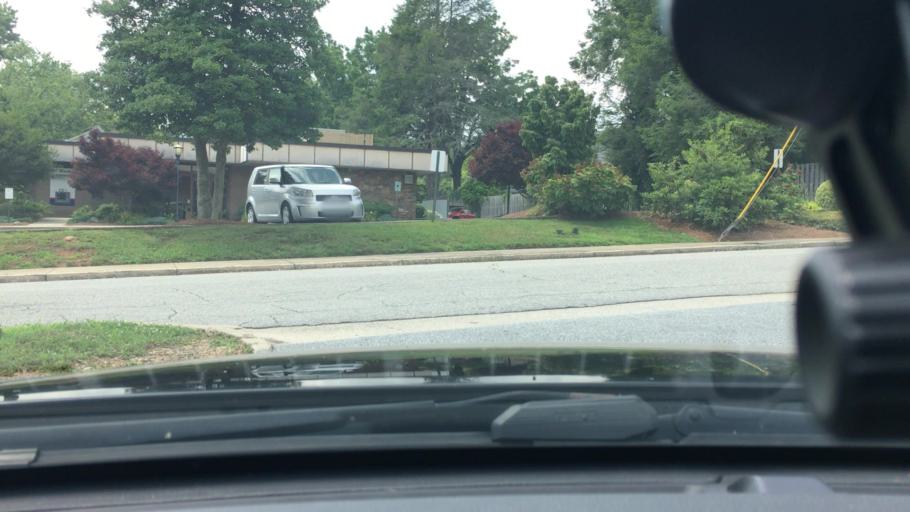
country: US
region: North Carolina
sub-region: Transylvania County
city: Brevard
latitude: 35.2349
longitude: -82.7363
